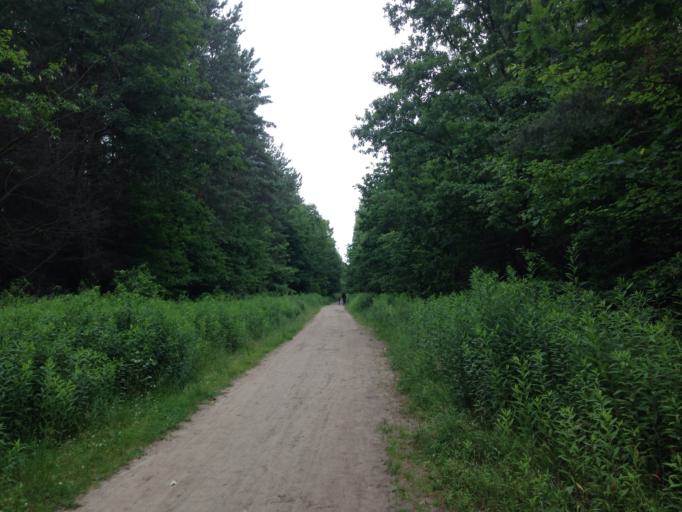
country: PL
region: Masovian Voivodeship
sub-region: Powiat warszawski zachodni
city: Babice
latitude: 52.2553
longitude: 20.8690
